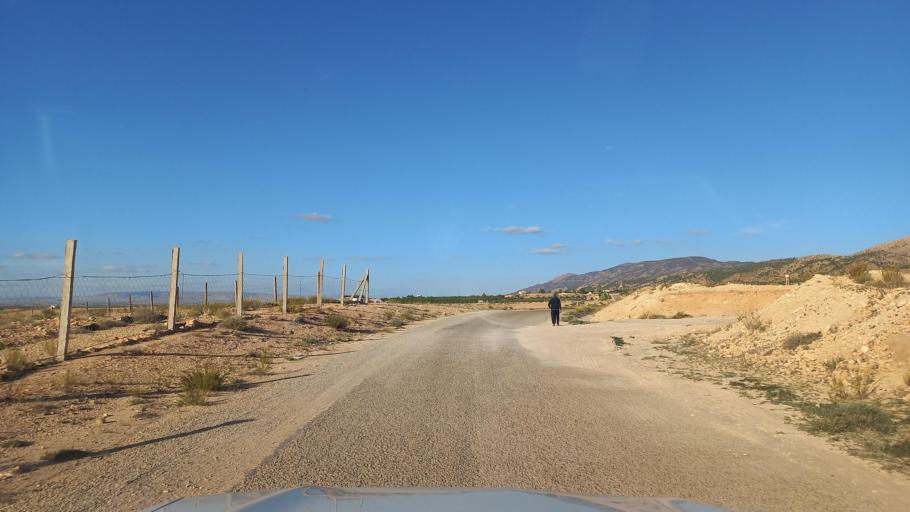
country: TN
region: Al Qasrayn
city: Sbiba
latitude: 35.3593
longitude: 9.1424
